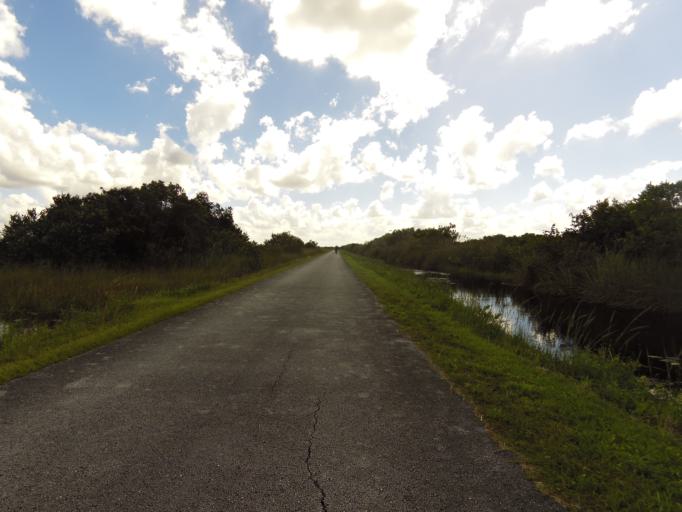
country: US
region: Florida
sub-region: Miami-Dade County
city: The Hammocks
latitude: 25.7218
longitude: -80.7667
